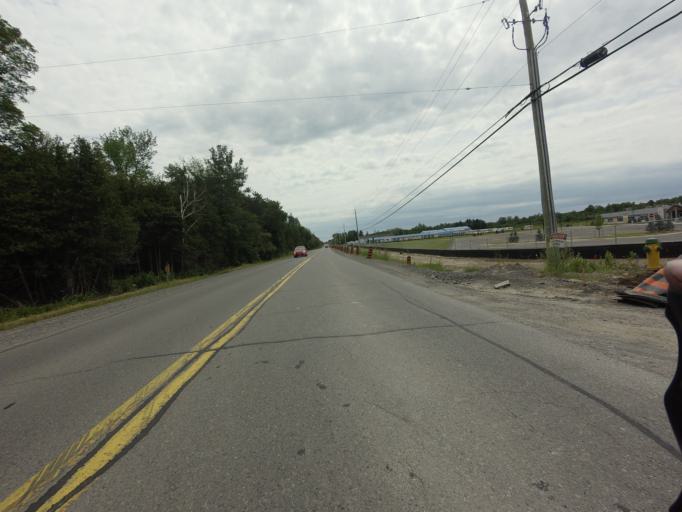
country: CA
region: Ontario
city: Bells Corners
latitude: 45.0317
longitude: -75.6624
